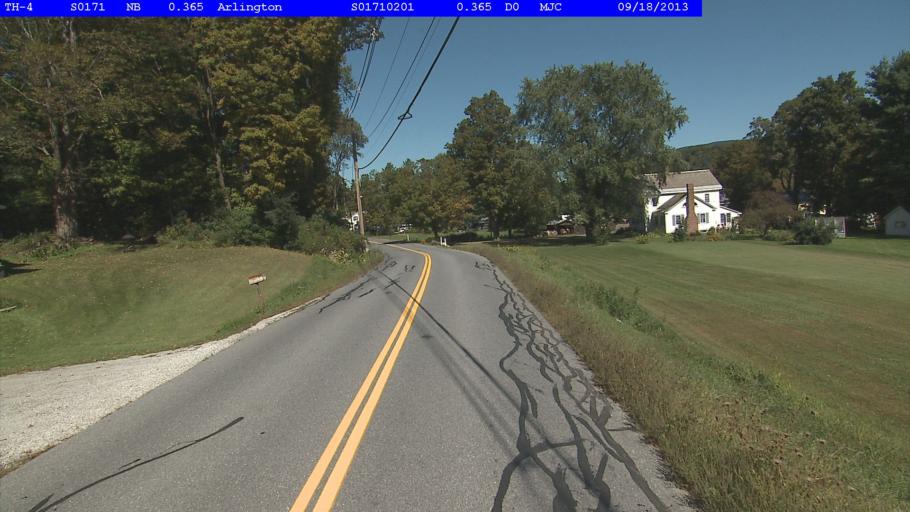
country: US
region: Vermont
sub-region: Bennington County
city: Arlington
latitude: 43.0584
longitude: -73.1479
